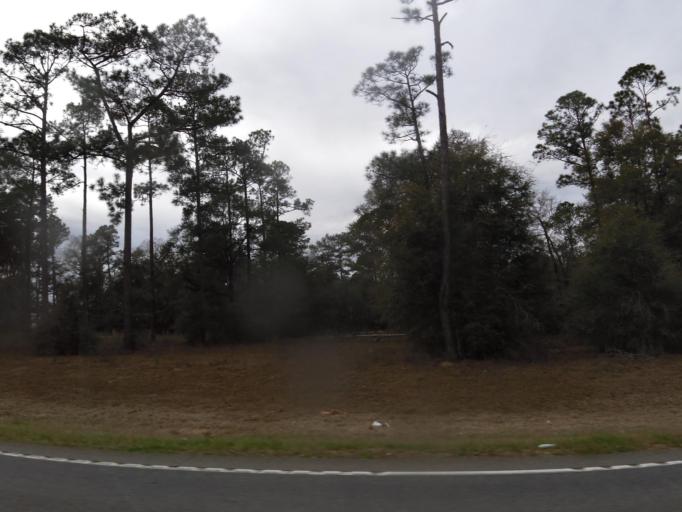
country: US
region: Georgia
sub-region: Randolph County
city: Shellman
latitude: 31.7765
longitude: -84.6050
